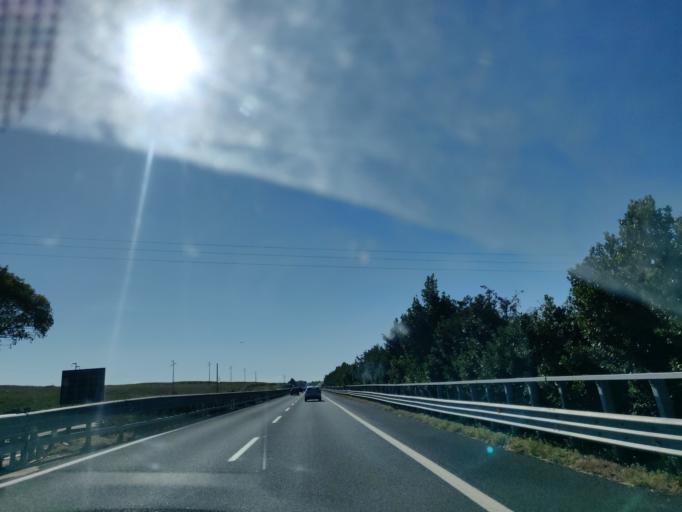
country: IT
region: Latium
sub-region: Citta metropolitana di Roma Capitale
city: Valcanneto
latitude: 41.9345
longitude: 12.1638
